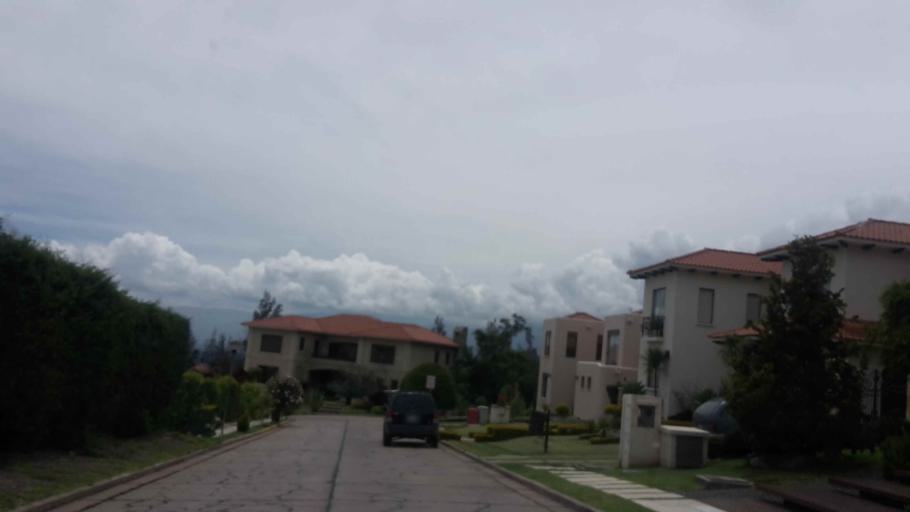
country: BO
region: Cochabamba
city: Cochabamba
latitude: -17.3380
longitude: -66.1864
